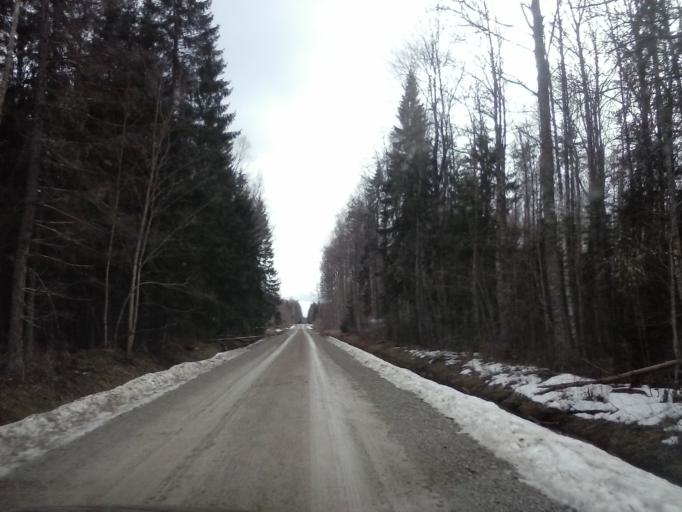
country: EE
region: Jogevamaa
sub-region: Mustvee linn
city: Mustvee
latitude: 59.0744
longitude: 26.8095
